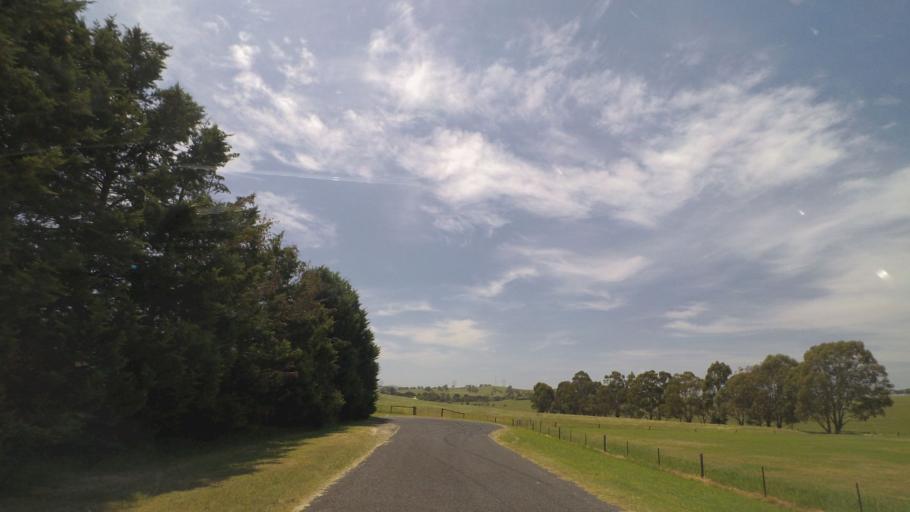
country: AU
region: Victoria
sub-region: Yarra Ranges
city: Chirnside Park
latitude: -37.7427
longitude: 145.3053
